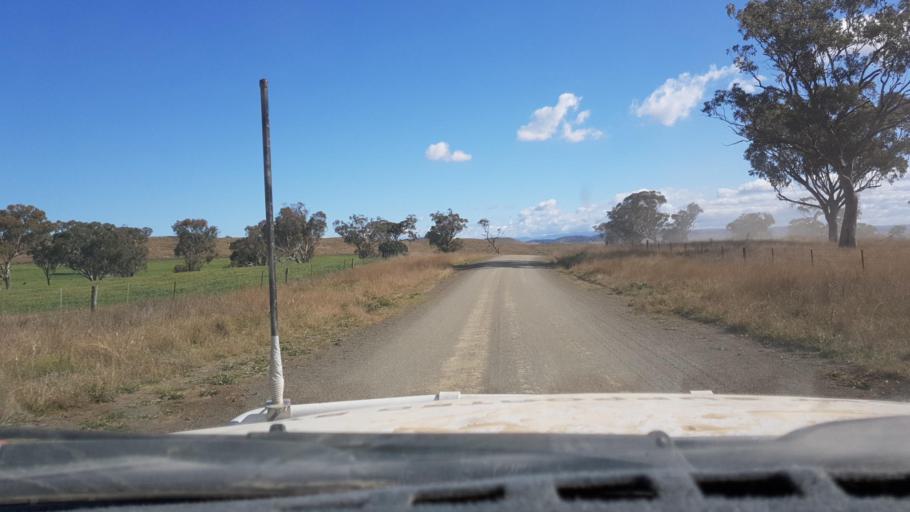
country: AU
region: New South Wales
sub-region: Narrabri
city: Blair Athol
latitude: -30.5446
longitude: 150.4532
